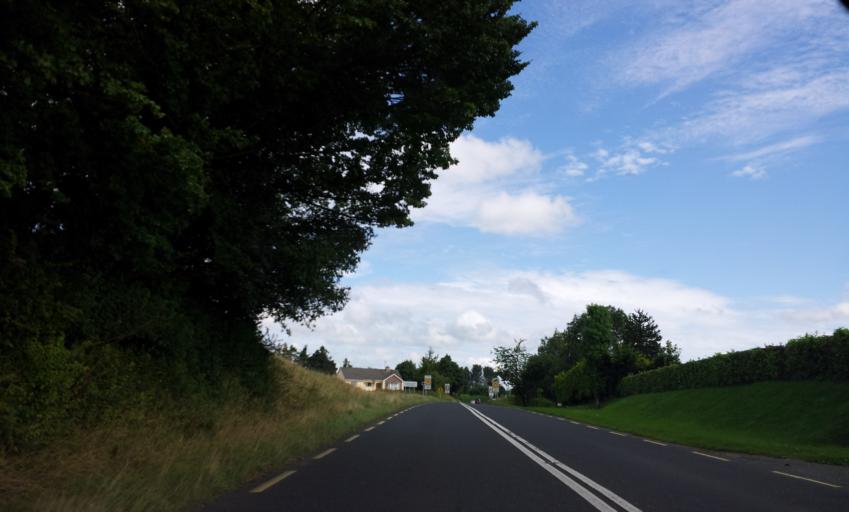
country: IE
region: Leinster
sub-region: Laois
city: Mountrath
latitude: 52.9903
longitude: -7.4866
